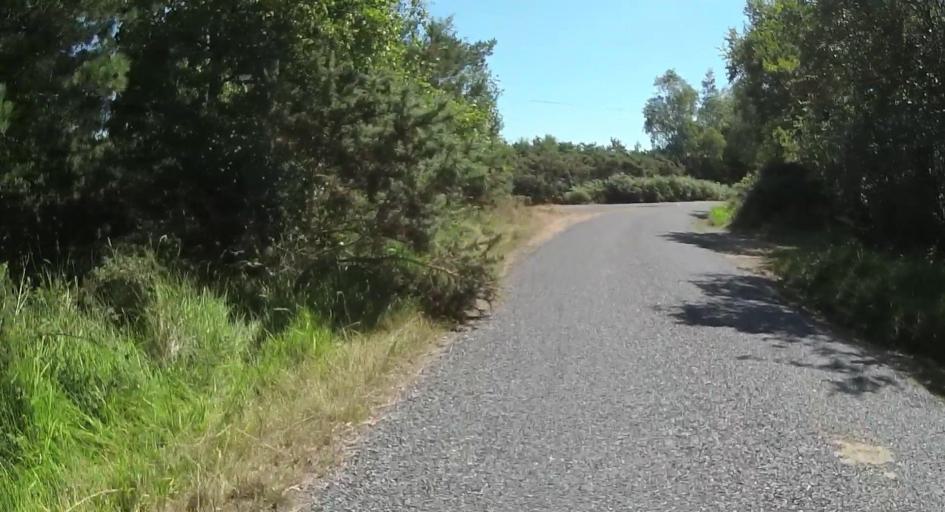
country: GB
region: England
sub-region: Dorset
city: Wareham
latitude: 50.6784
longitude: -2.0640
